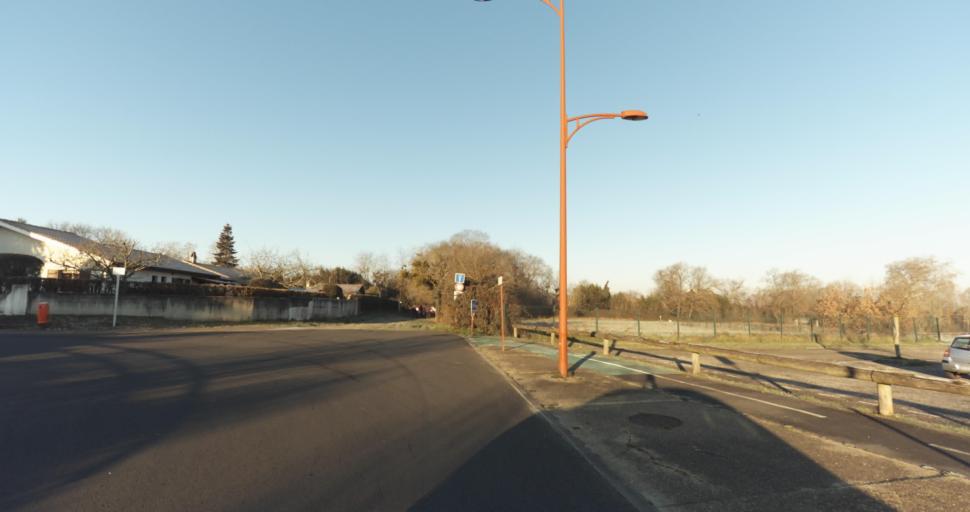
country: FR
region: Aquitaine
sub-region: Departement de la Gironde
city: Carbon-Blanc
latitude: 44.9100
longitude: -0.5026
